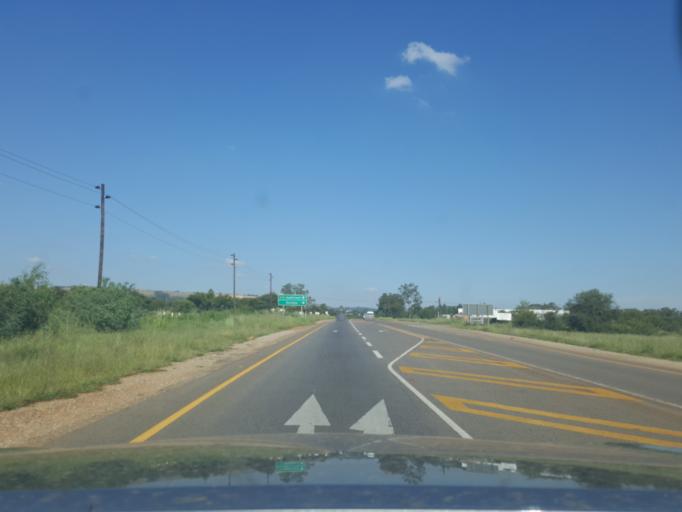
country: ZA
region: Gauteng
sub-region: City of Tshwane Metropolitan Municipality
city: Cullinan
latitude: -25.7597
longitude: 28.4132
